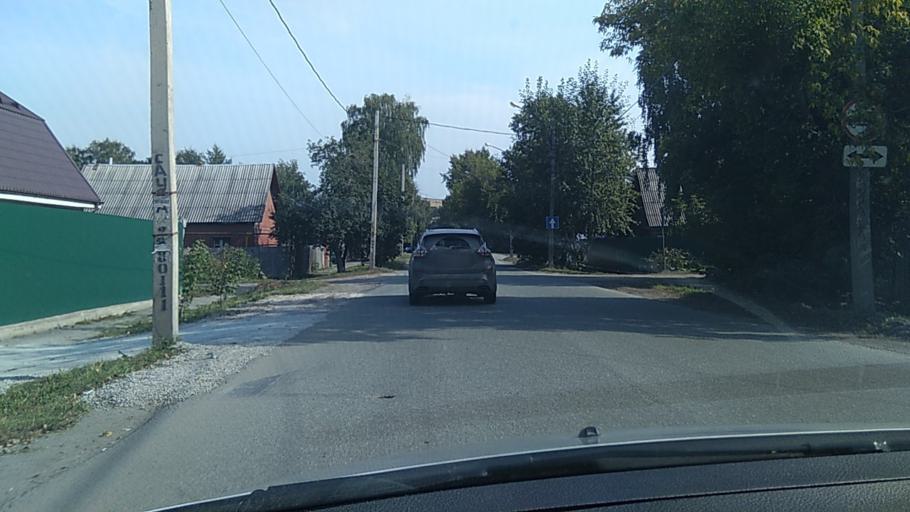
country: RU
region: Sverdlovsk
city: Yekaterinburg
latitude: 56.8820
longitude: 60.5523
